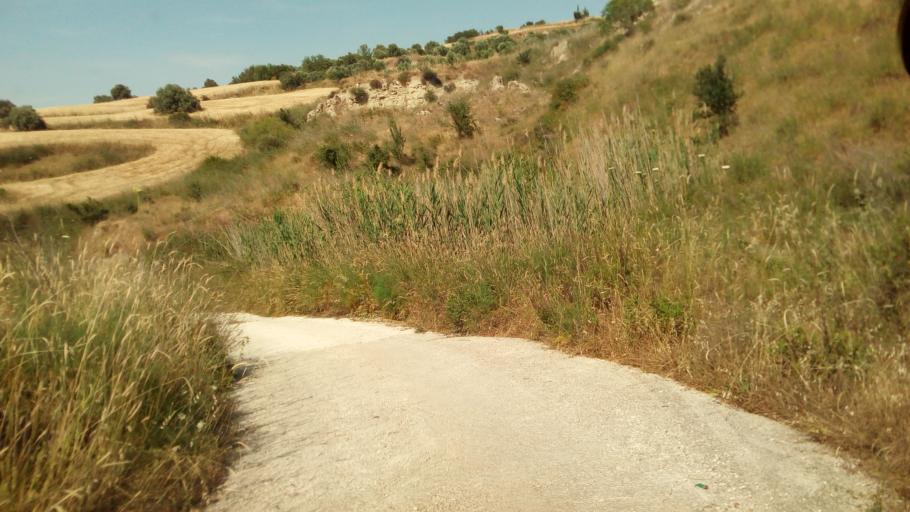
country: CY
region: Pafos
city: Tala
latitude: 34.9372
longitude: 32.5314
